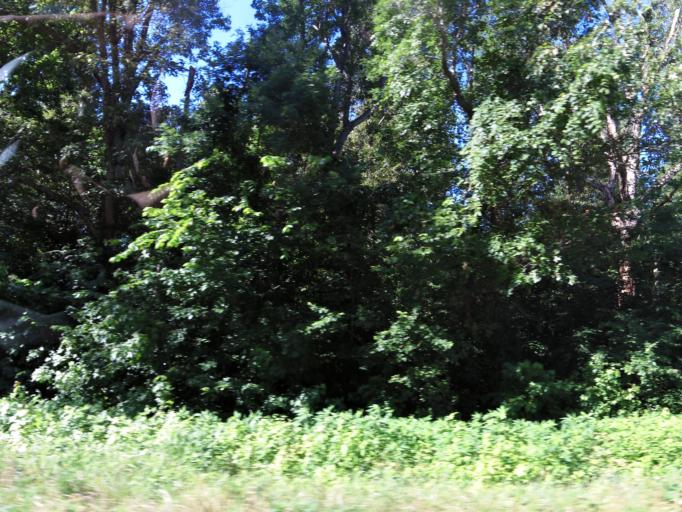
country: US
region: Arkansas
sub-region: Clay County
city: Piggott
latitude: 36.4331
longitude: -90.3019
